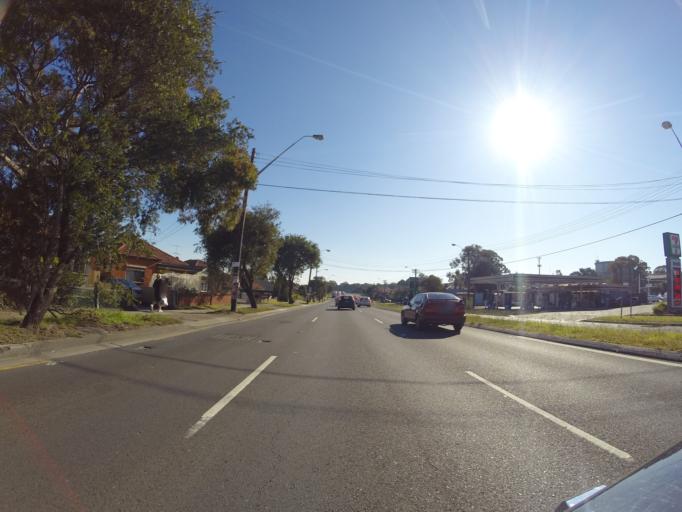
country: AU
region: New South Wales
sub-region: Canterbury
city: Roselands
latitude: -33.9341
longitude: 151.0734
